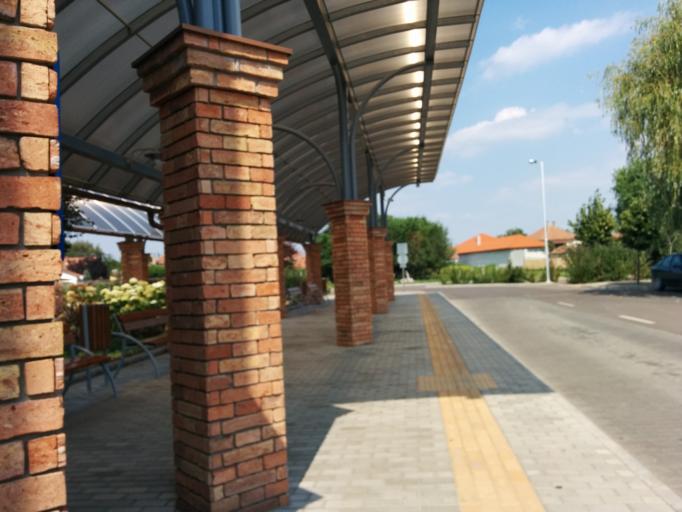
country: HU
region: Csongrad
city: Sandorfalva
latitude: 46.3665
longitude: 20.1059
